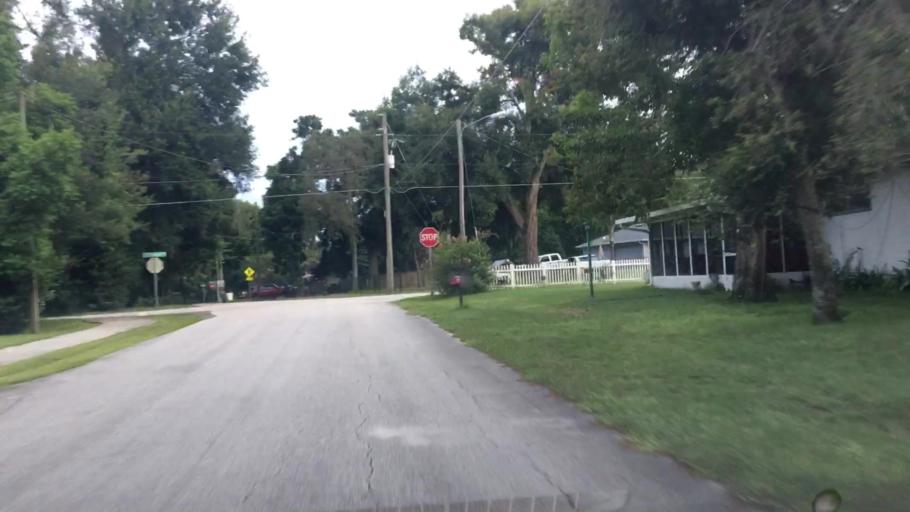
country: US
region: Florida
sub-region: Volusia County
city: DeBary
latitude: 28.8812
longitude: -81.3067
